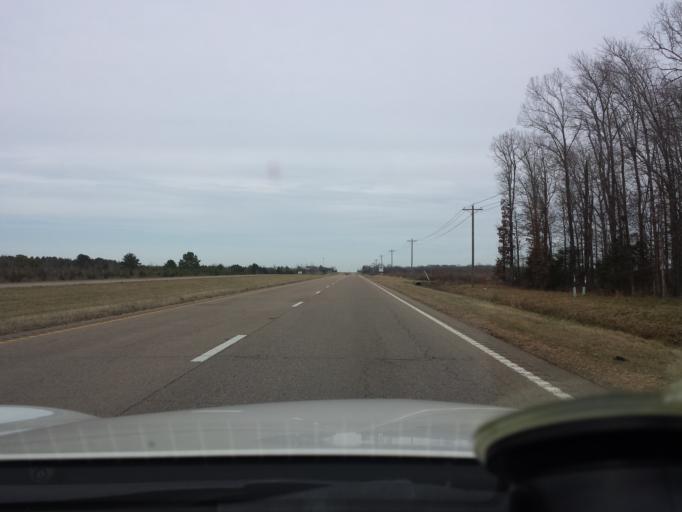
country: US
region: Mississippi
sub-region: Clay County
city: West Point
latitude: 33.5133
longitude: -88.6588
